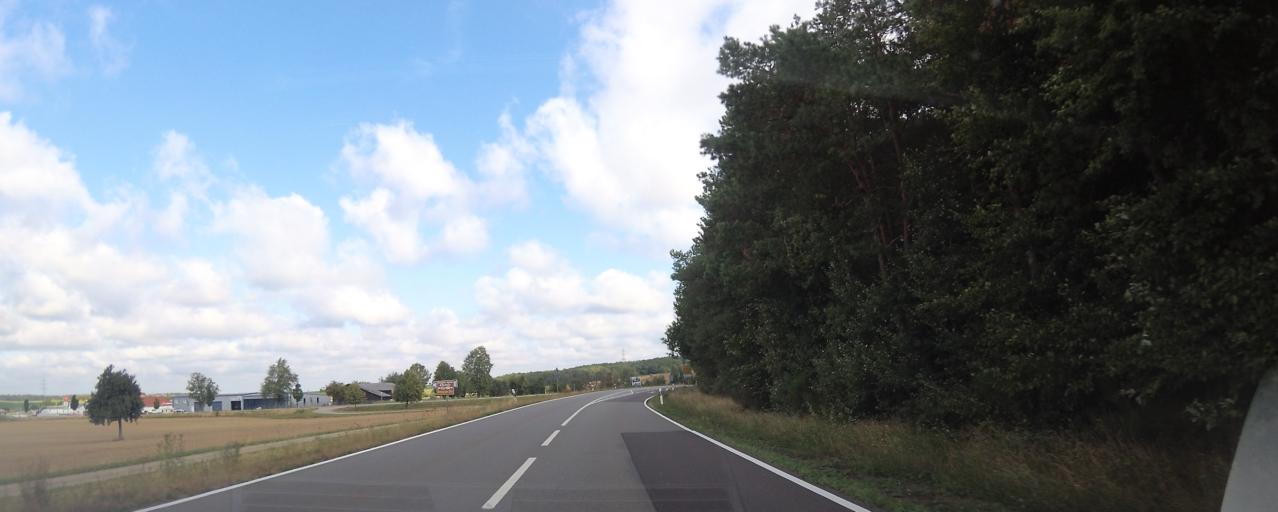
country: DE
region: Rheinland-Pfalz
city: Zemmer
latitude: 49.8962
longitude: 6.7071
